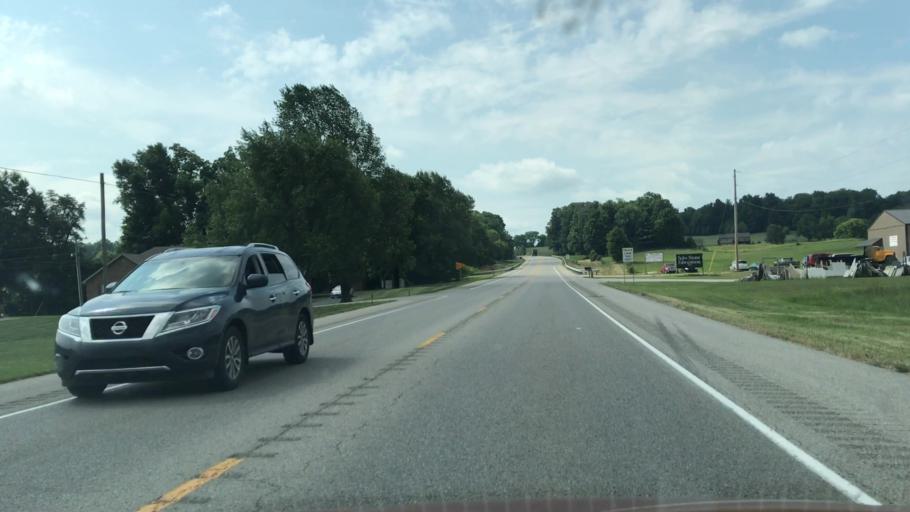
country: US
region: Kentucky
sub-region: Barren County
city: Cave City
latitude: 37.0908
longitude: -85.9723
